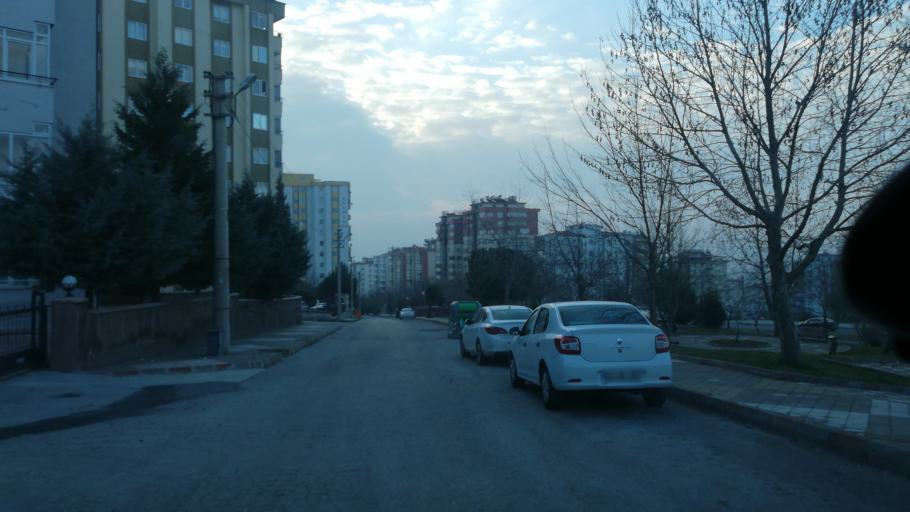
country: TR
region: Kahramanmaras
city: Kahramanmaras
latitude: 37.5956
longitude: 36.8917
